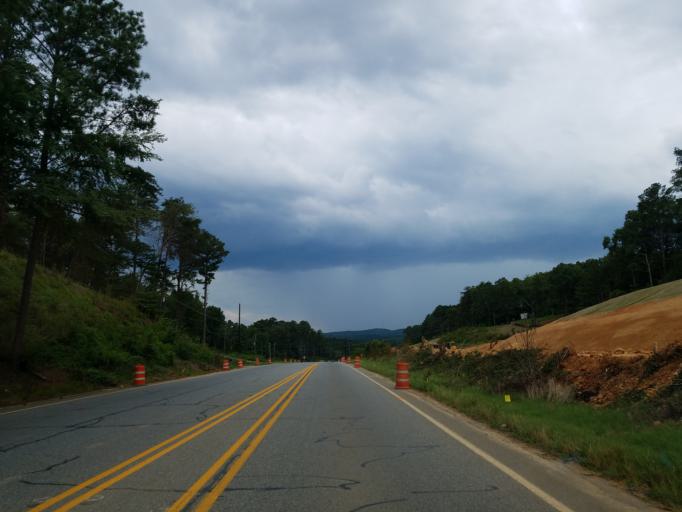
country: US
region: Georgia
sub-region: Bartow County
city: Adairsville
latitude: 34.3726
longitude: -84.9909
